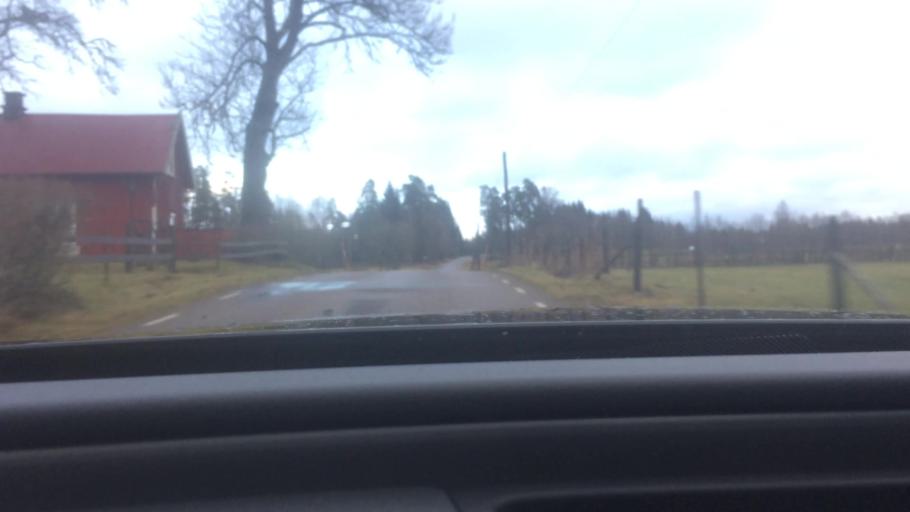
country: SE
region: Vaestra Goetaland
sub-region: Falkopings Kommun
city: Falkoeping
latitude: 57.9939
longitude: 13.4722
